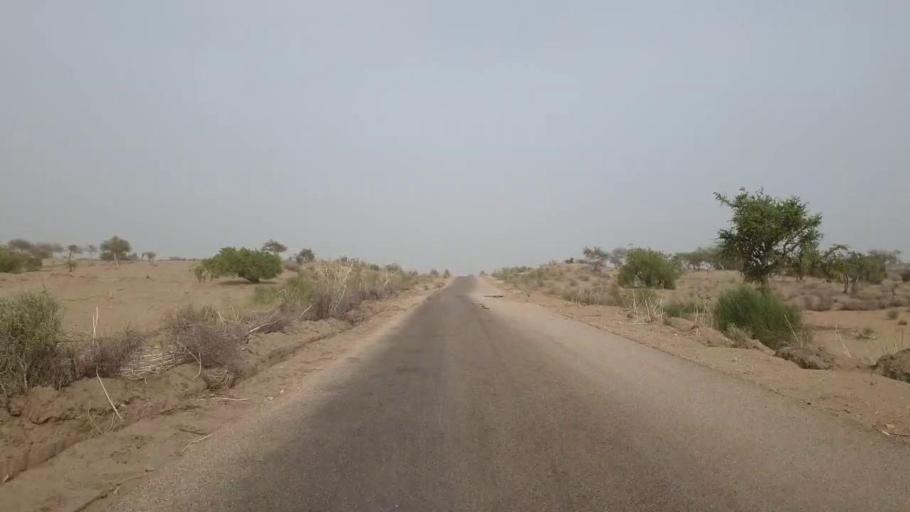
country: PK
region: Sindh
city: Islamkot
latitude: 24.5628
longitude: 70.3366
